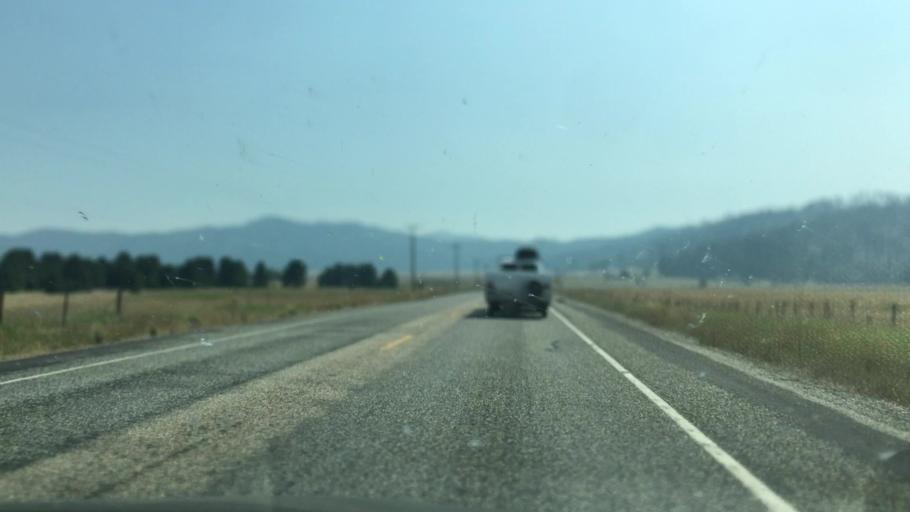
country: US
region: Idaho
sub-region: Valley County
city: Cascade
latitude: 44.3424
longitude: -116.0286
